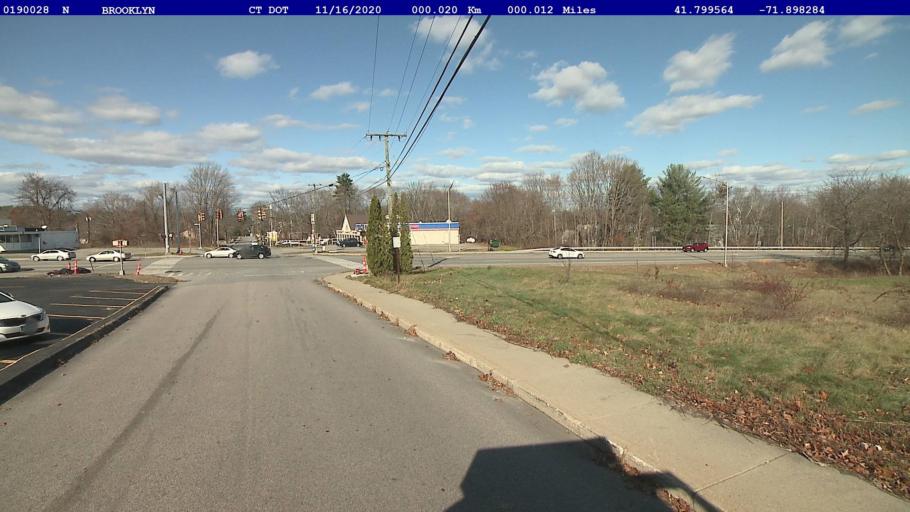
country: US
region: Connecticut
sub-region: Windham County
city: East Brooklyn
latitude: 41.7996
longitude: -71.8983
